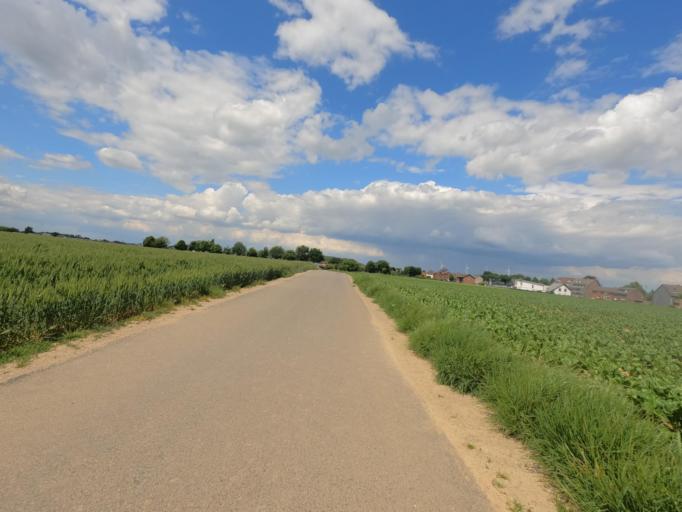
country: DE
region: North Rhine-Westphalia
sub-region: Regierungsbezirk Koln
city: Ubach-Palenberg
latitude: 50.9100
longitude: 6.1273
